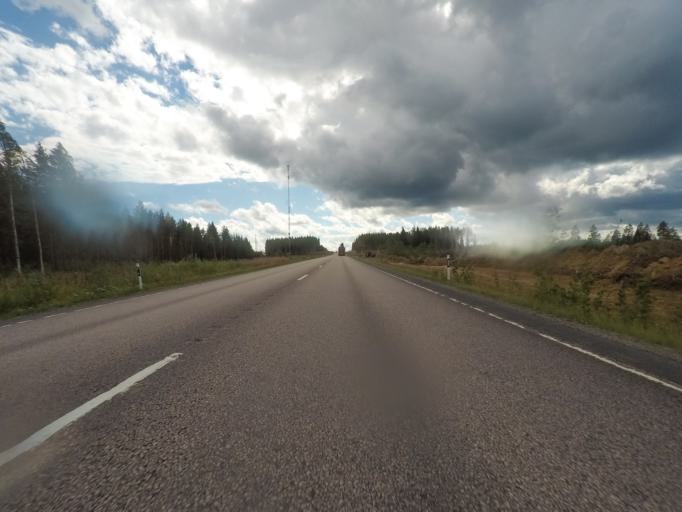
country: FI
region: Central Finland
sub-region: Joutsa
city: Leivonmaeki
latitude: 61.8795
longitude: 26.1107
